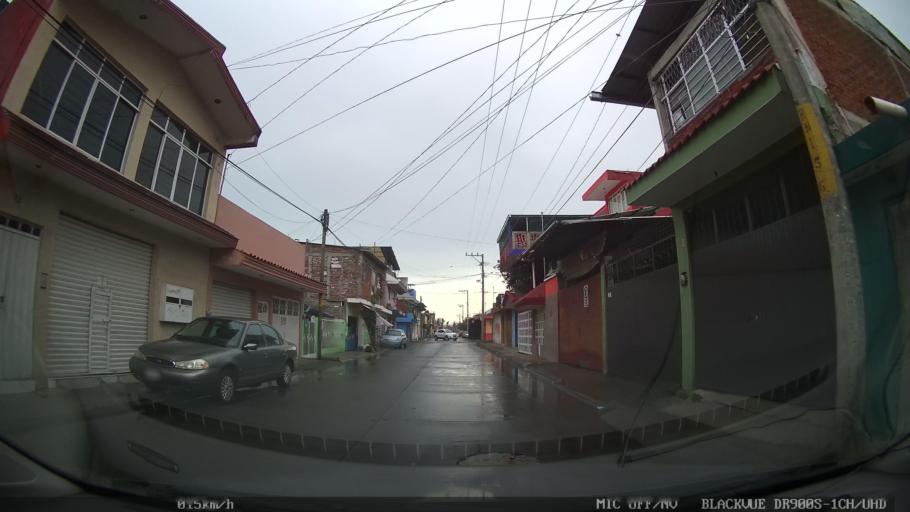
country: MX
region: Michoacan
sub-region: Uruapan
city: Santa Rosa (Santa Barbara)
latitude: 19.4025
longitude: -102.0257
